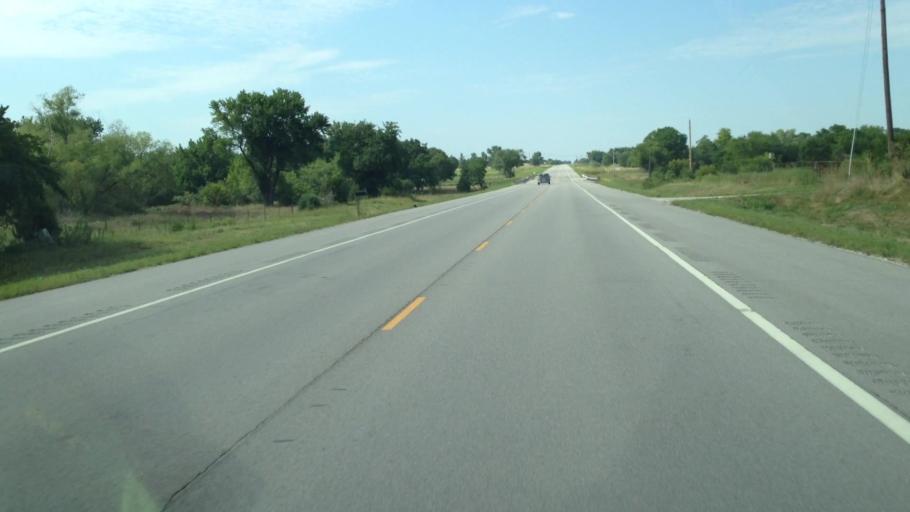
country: US
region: Kansas
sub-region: Labette County
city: Parsons
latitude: 37.2704
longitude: -95.2673
